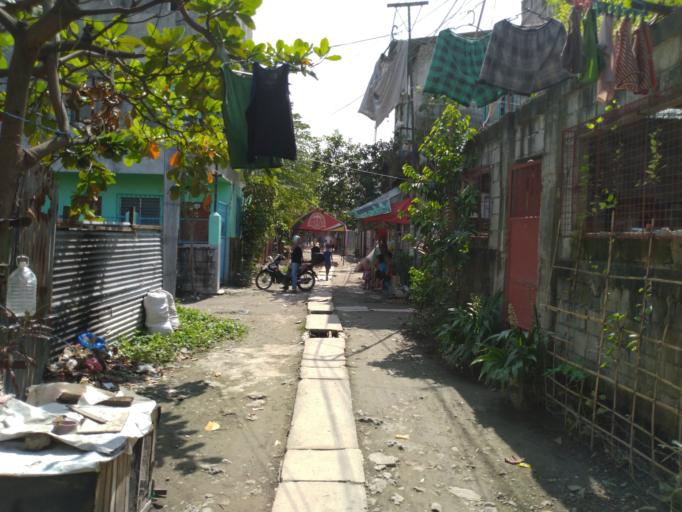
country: PH
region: Calabarzon
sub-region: Province of Rizal
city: Taytay
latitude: 14.5397
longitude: 121.1116
